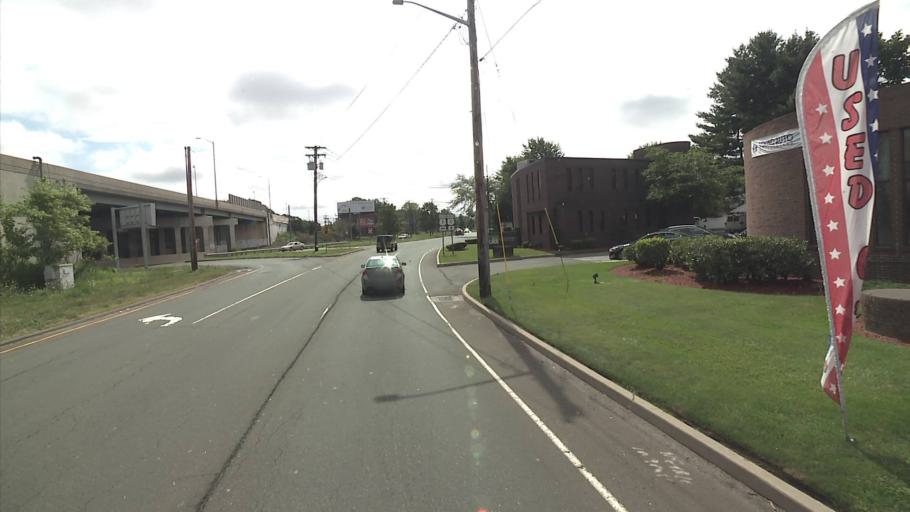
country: US
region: Connecticut
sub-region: New Haven County
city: East Haven
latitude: 41.2847
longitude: -72.8754
